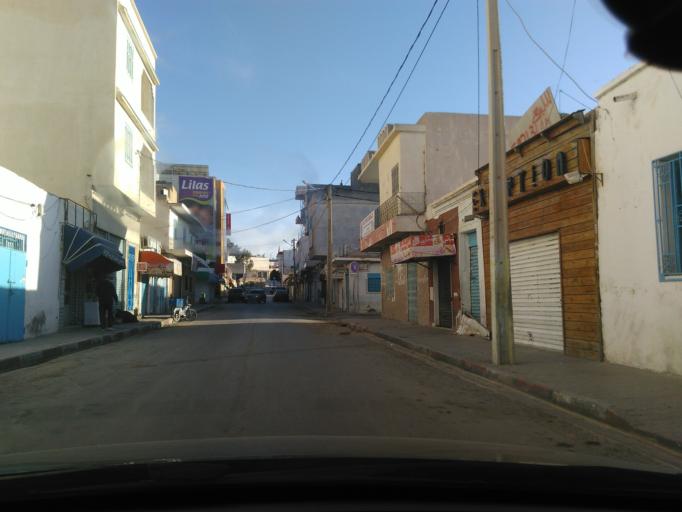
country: TN
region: Tataouine
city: Tataouine
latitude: 32.9286
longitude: 10.4484
